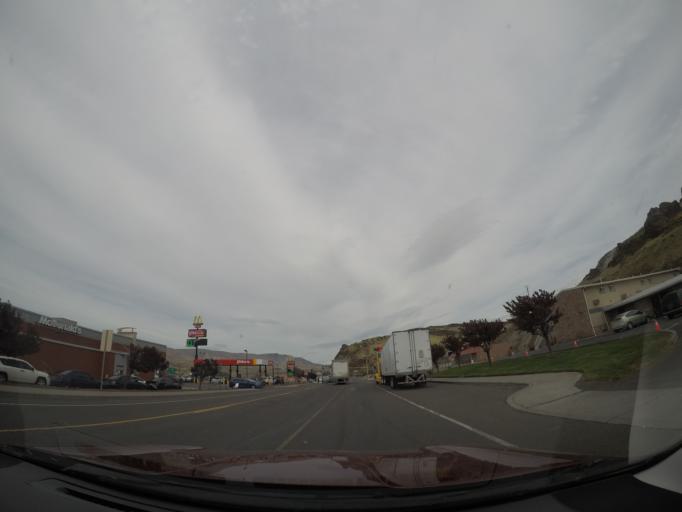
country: US
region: Washington
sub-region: Klickitat County
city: Goldendale
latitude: 45.6690
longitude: -120.8349
